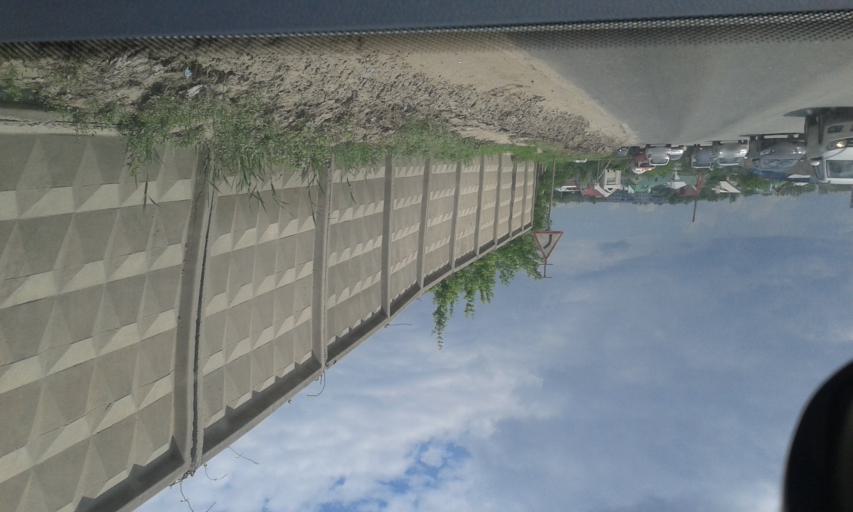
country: RU
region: Volgograd
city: Volgograd
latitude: 48.7665
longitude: 44.5122
